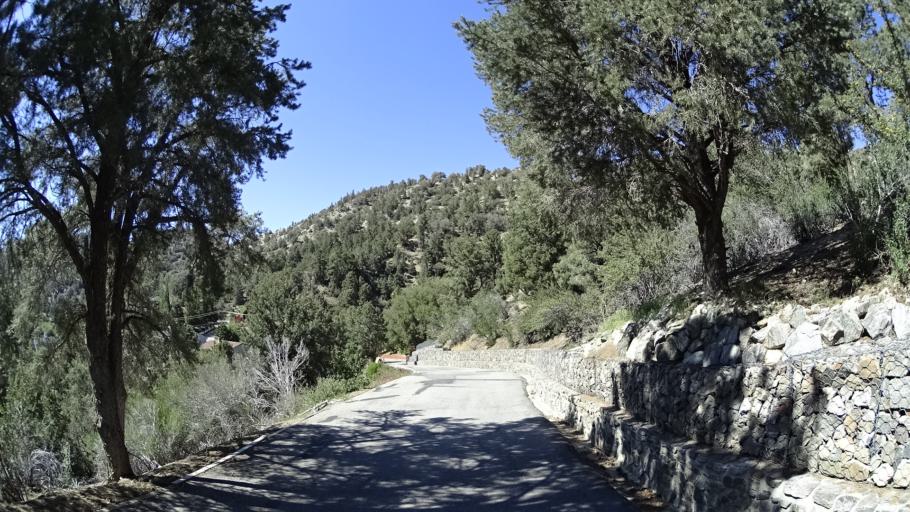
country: US
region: California
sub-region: San Bernardino County
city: Wrightwood
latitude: 34.3636
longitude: -117.6343
